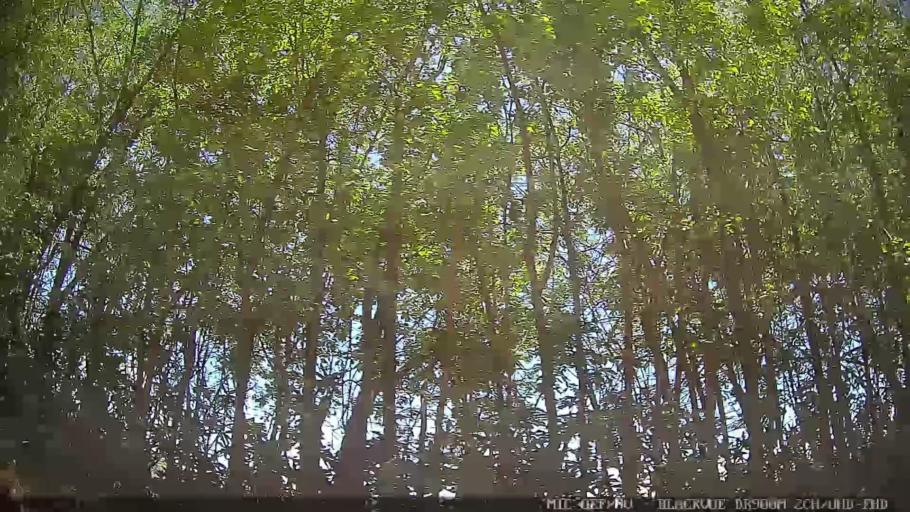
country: BR
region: Sao Paulo
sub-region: Jaguariuna
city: Jaguariuna
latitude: -22.7208
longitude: -46.9970
